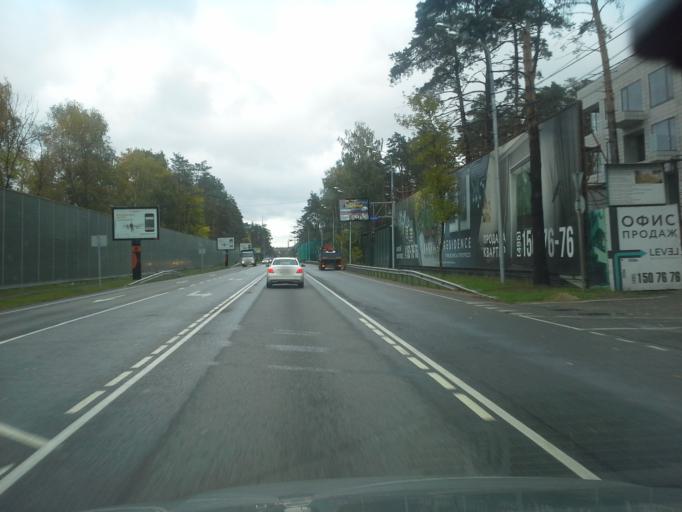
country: RU
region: Moskovskaya
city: Barvikha
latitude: 55.7443
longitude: 37.2867
